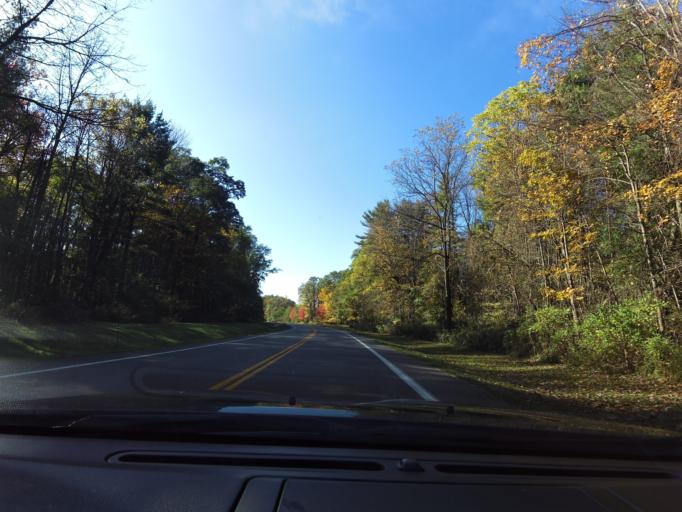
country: US
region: New York
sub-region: Livingston County
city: Mount Morris
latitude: 42.7107
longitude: -77.9359
